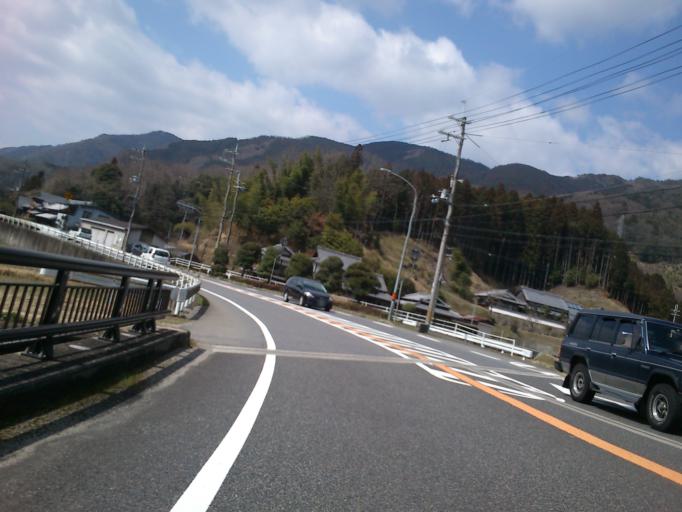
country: JP
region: Mie
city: Ueno-ebisumachi
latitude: 34.7763
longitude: 136.0176
